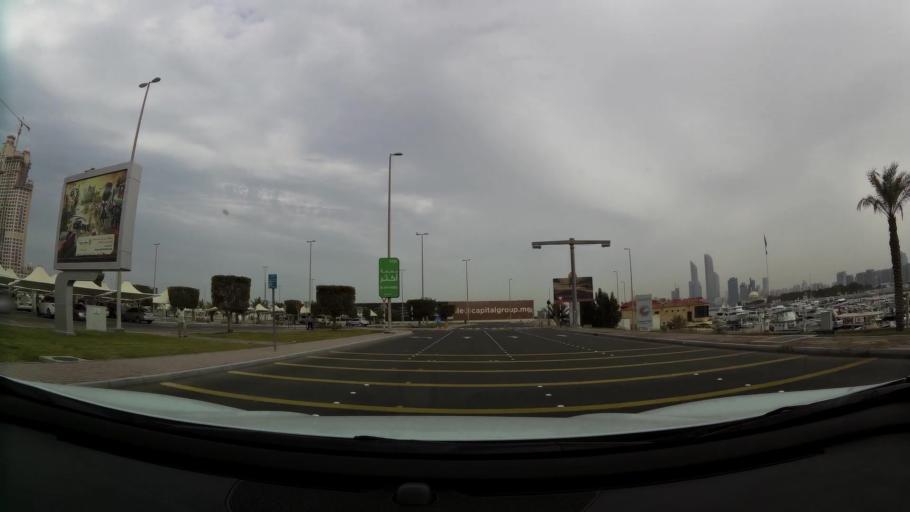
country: AE
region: Abu Dhabi
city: Abu Dhabi
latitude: 24.4757
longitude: 54.3239
